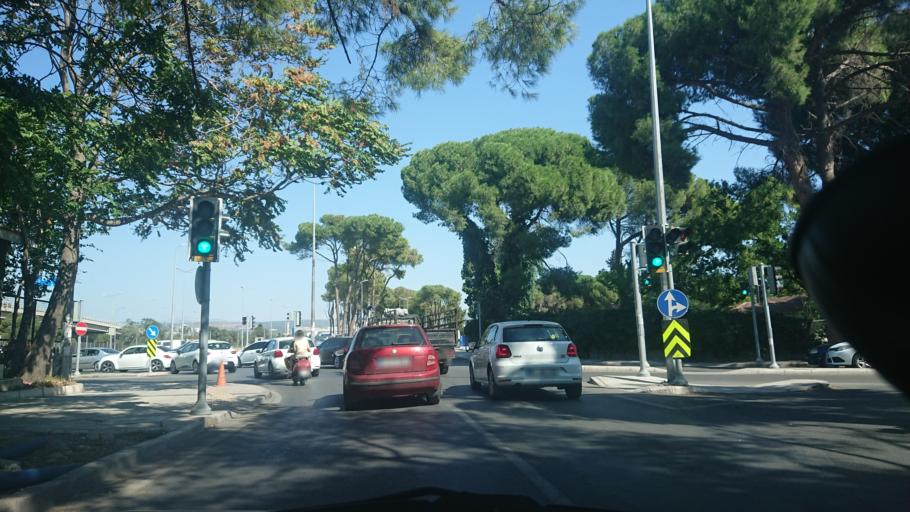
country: TR
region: Izmir
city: Bornova
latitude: 38.4584
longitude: 27.2161
